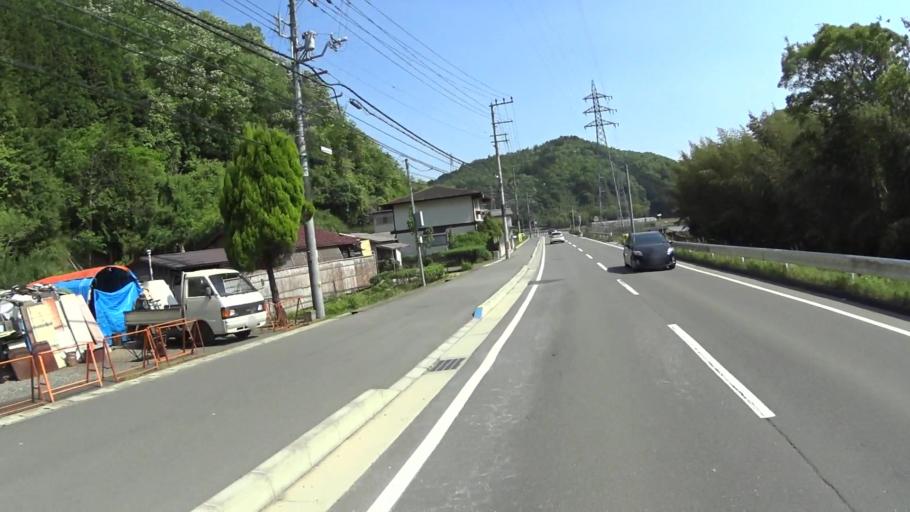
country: JP
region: Kyoto
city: Kameoka
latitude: 35.1224
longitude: 135.5064
